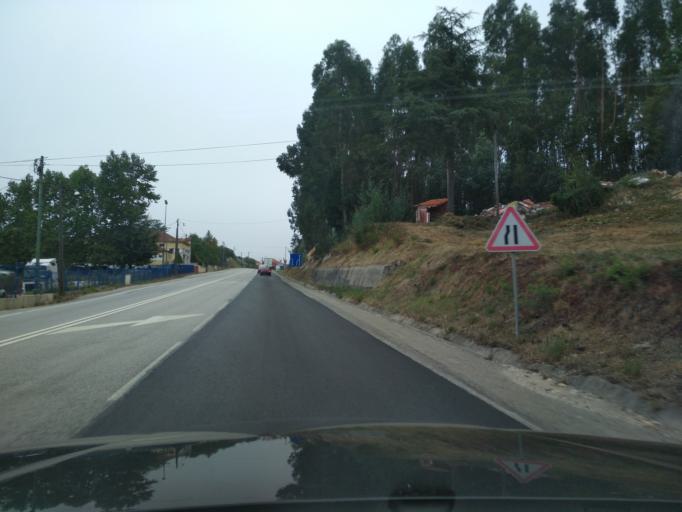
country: PT
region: Aveiro
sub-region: Mealhada
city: Pampilhosa do Botao
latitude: 40.3023
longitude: -8.4473
